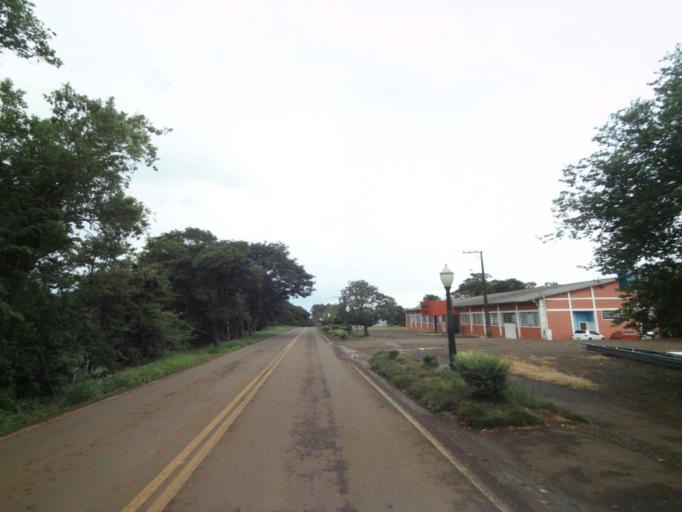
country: BR
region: Parana
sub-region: Guaraniacu
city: Guaraniacu
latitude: -25.0965
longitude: -52.8793
